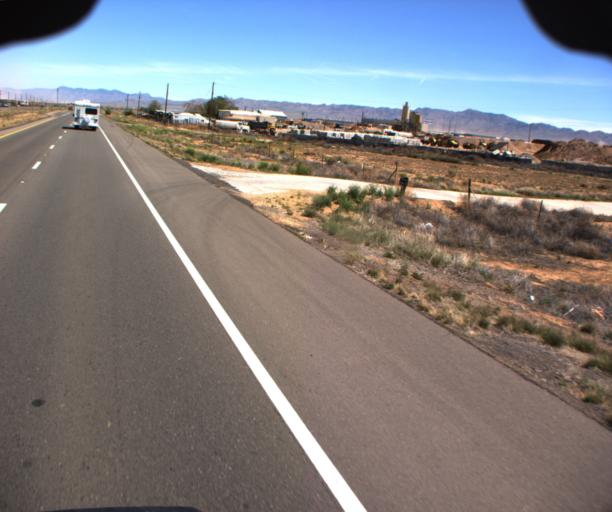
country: US
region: Arizona
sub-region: Mohave County
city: New Kingman-Butler
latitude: 35.2519
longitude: -113.9772
